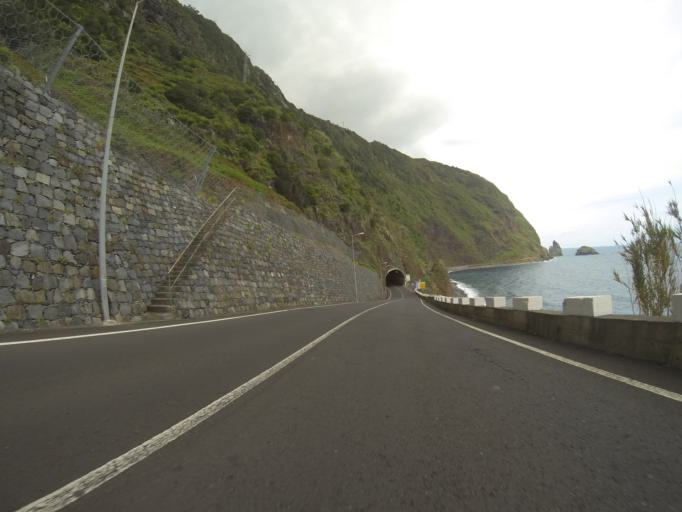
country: PT
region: Madeira
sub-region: Porto Moniz
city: Porto Moniz
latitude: 32.8480
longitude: -17.1500
